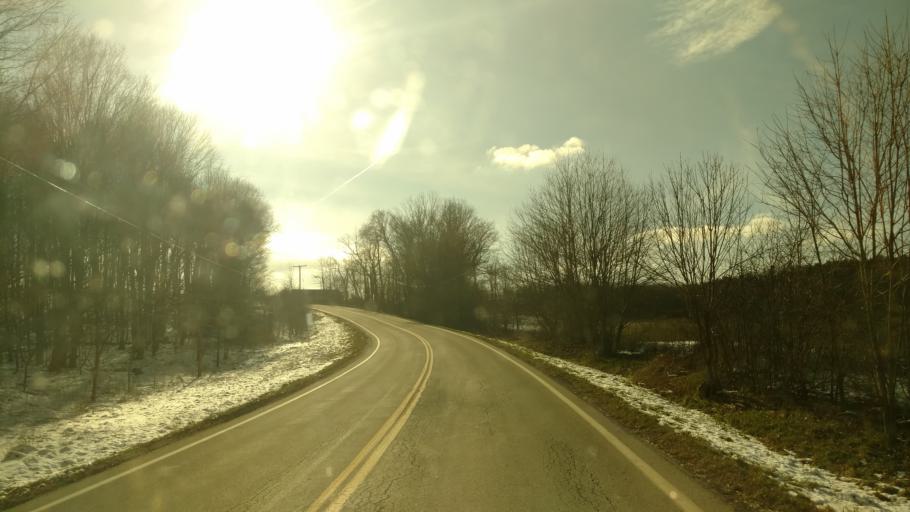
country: US
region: Ohio
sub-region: Ashland County
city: Loudonville
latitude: 40.6775
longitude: -82.2917
